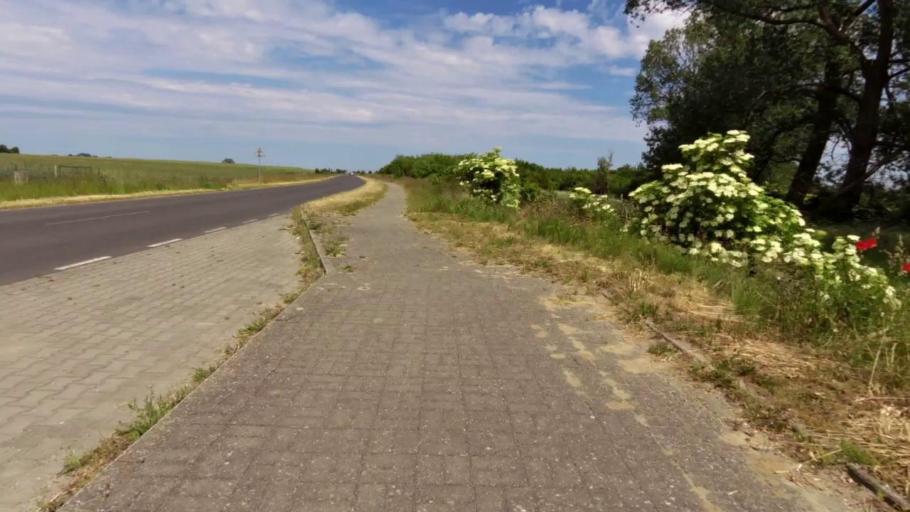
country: PL
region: West Pomeranian Voivodeship
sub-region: Powiat kamienski
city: Kamien Pomorski
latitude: 53.9597
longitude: 14.6862
